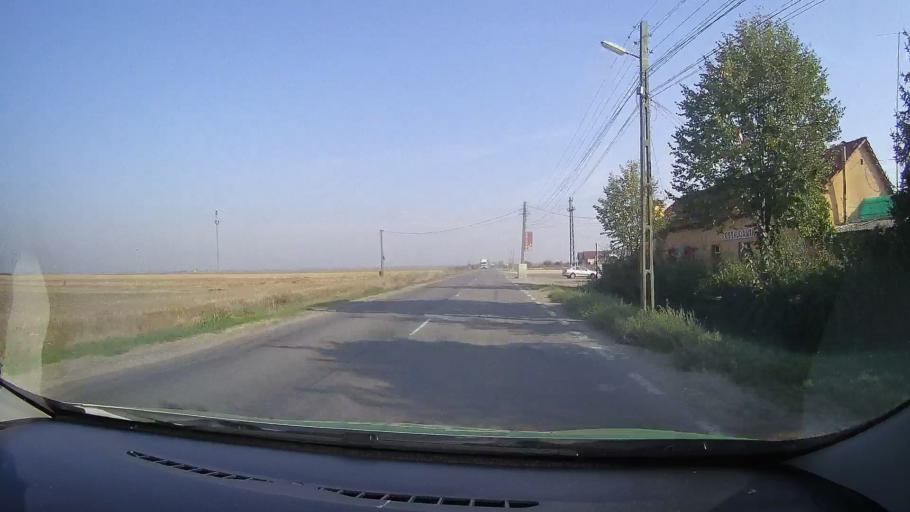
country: RO
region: Arad
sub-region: Comuna Pilu
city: Pilu
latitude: 46.5844
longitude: 21.3442
